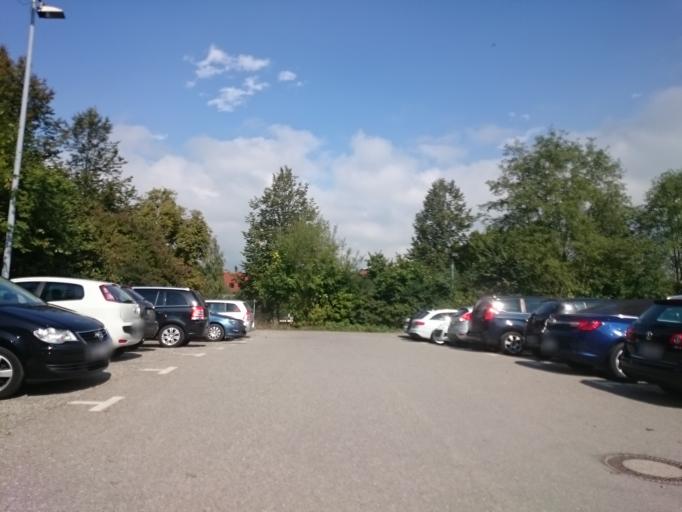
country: DE
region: Bavaria
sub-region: Swabia
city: Kempten (Allgaeu)
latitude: 47.7290
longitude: 10.3145
